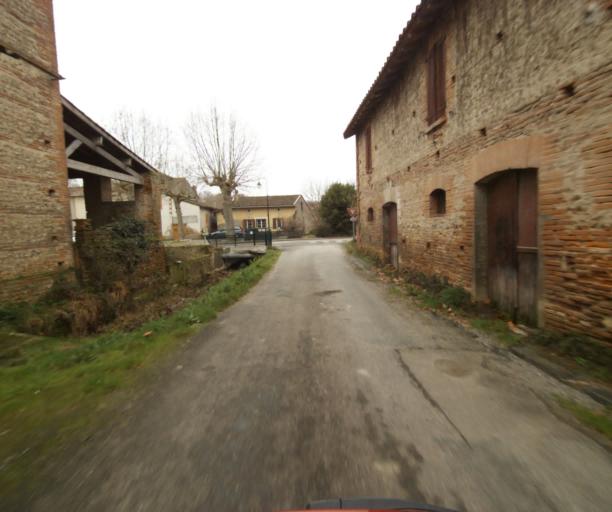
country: FR
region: Midi-Pyrenees
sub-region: Departement de la Haute-Garonne
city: Gaillac-Toulza
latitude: 43.2696
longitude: 1.5124
